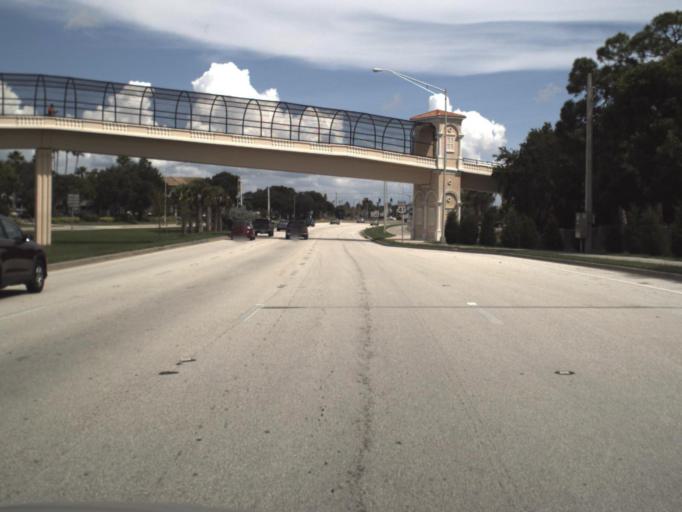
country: US
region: Florida
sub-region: Sarasota County
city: Nokomis
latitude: 27.1085
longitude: -82.4429
